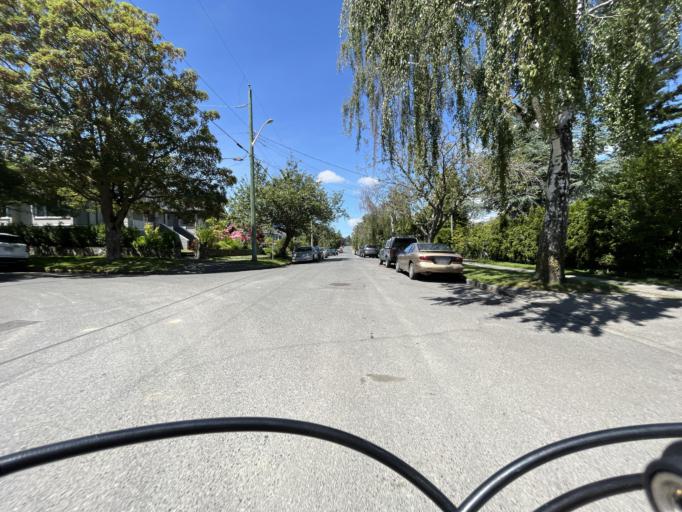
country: CA
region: British Columbia
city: Victoria
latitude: 48.4410
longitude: -123.3919
